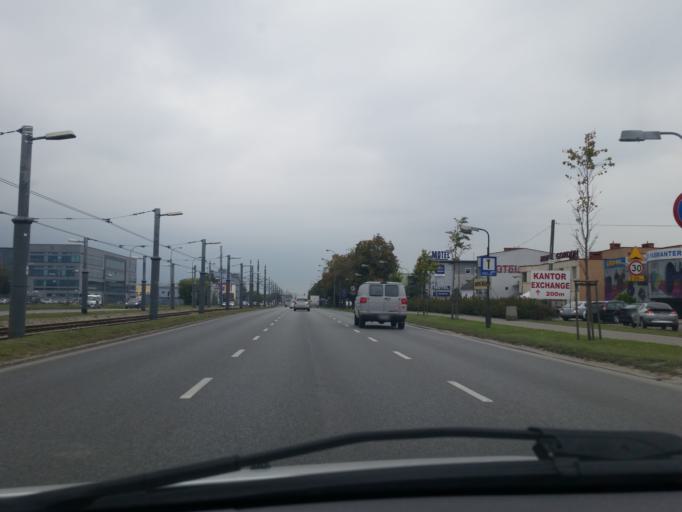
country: PL
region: Masovian Voivodeship
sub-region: Warszawa
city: Wlochy
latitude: 52.1824
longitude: 20.9503
